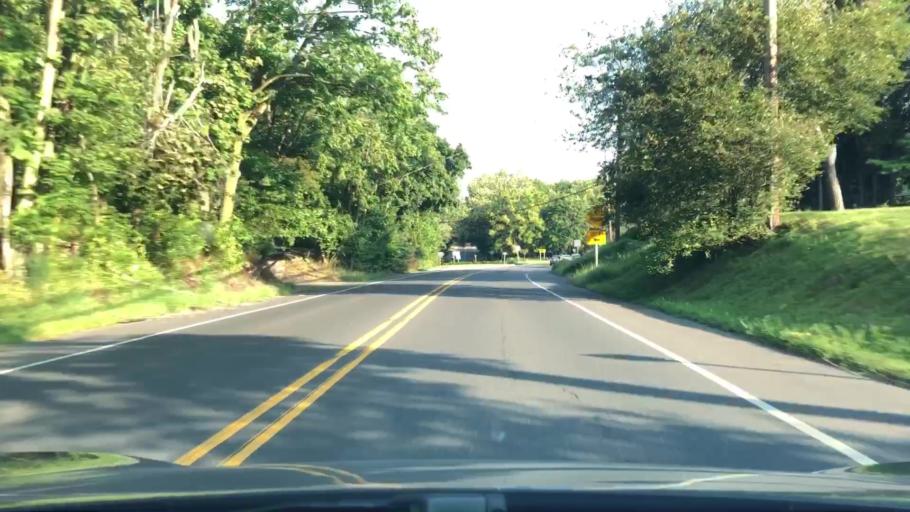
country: US
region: New Jersey
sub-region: Mercer County
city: Pennington
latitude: 40.3150
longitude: -74.7874
